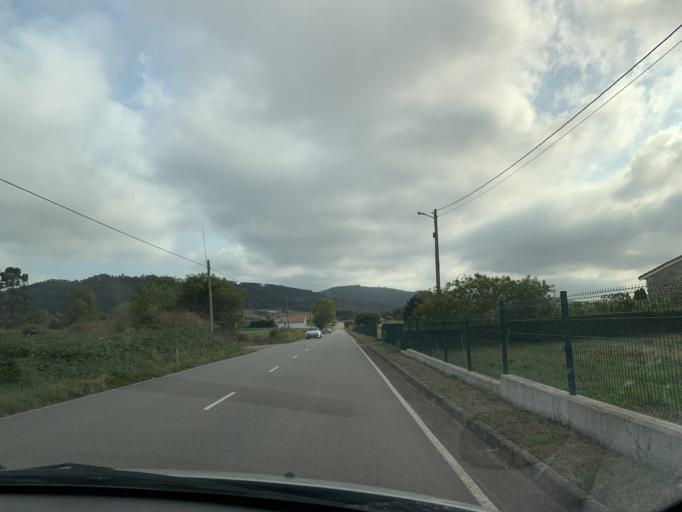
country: ES
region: Asturias
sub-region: Province of Asturias
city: Villaviciosa
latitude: 43.5276
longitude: -5.4331
